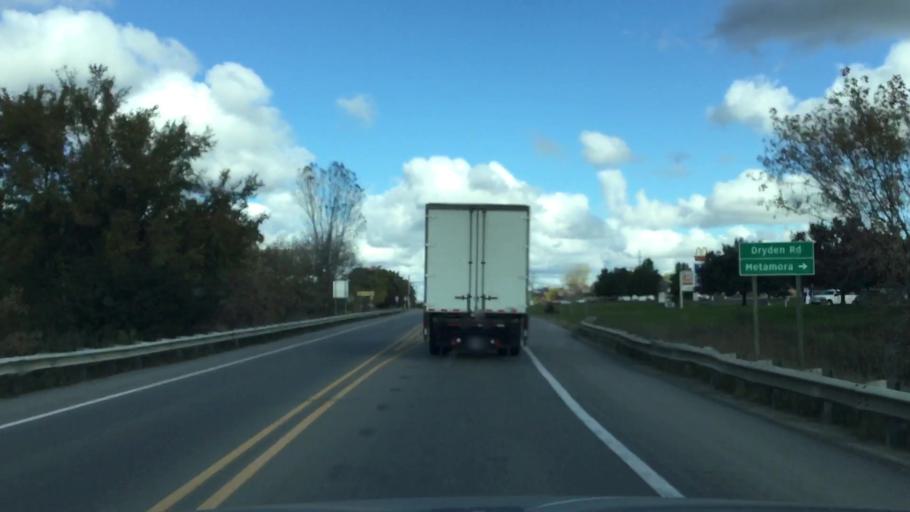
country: US
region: Michigan
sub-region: Lapeer County
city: Lapeer
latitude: 42.9417
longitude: -83.3135
